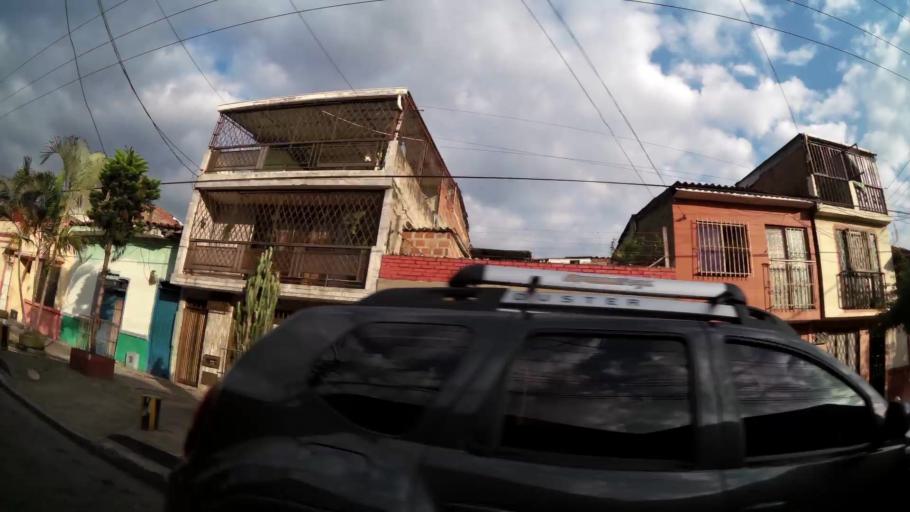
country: CO
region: Valle del Cauca
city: Cali
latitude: 3.4563
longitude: -76.5164
